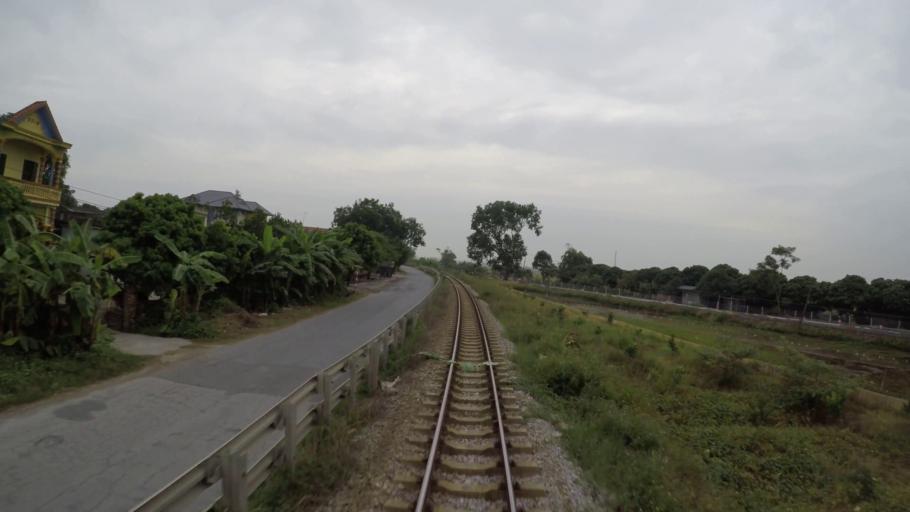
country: VN
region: Hung Yen
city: Ban Yen Nhan
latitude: 20.9694
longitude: 106.1028
